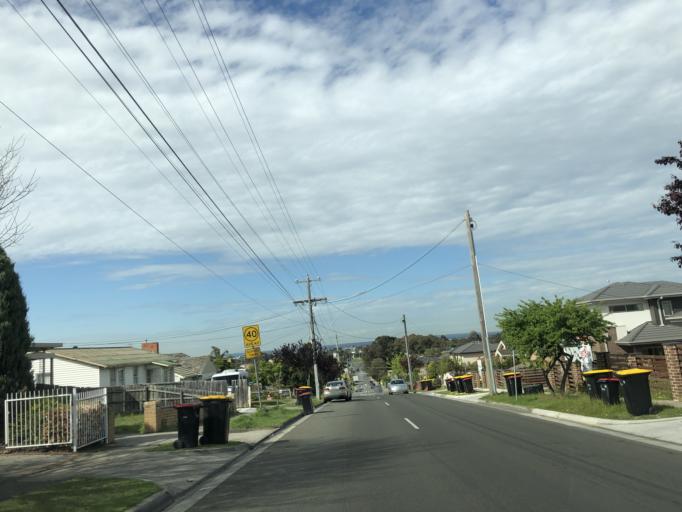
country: AU
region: Victoria
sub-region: Greater Dandenong
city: Dandenong
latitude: -37.9792
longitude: 145.2015
